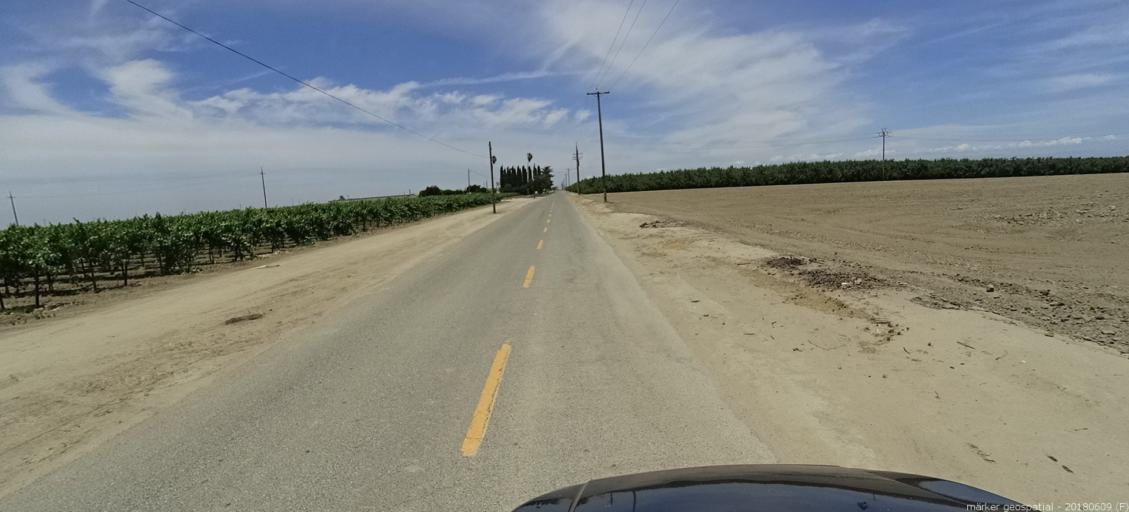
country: US
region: California
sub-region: Madera County
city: Parkwood
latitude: 36.9150
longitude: -120.1015
